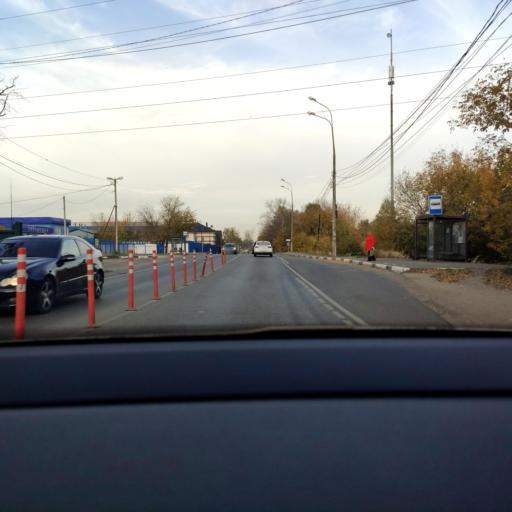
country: RU
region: Moskovskaya
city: Pirogovskiy
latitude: 55.9736
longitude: 37.7295
